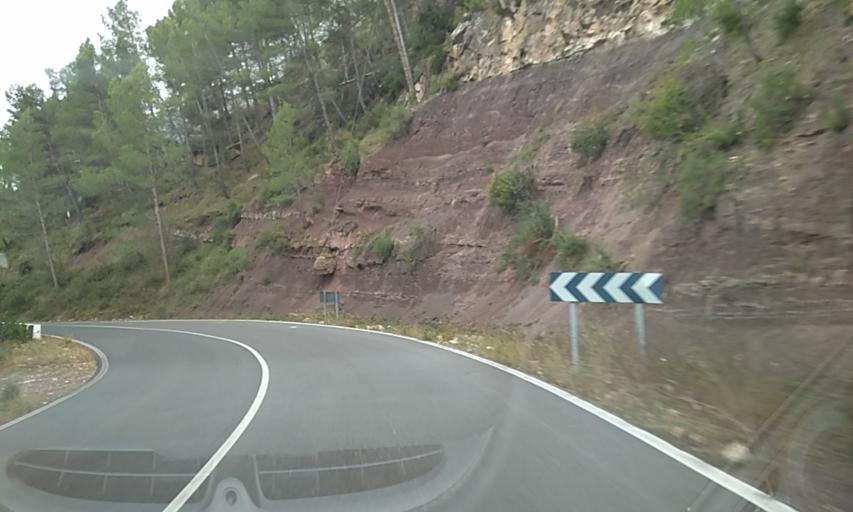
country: ES
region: Valencia
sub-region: Provincia de Castello
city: Puebla de Arenoso
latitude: 40.0866
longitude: -0.5563
